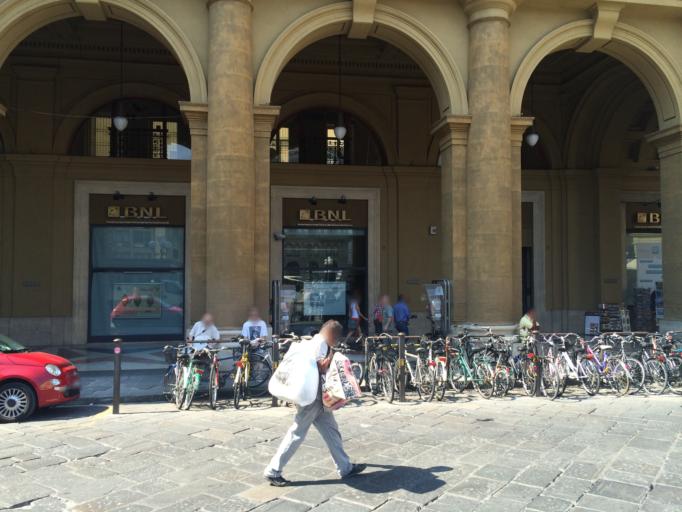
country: IT
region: Tuscany
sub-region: Province of Florence
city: Florence
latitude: 43.7712
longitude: 11.2537
